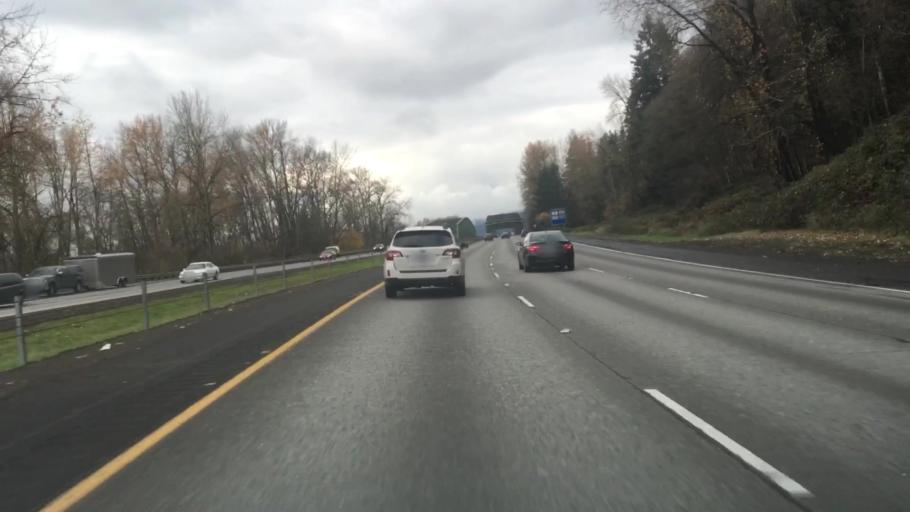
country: US
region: Washington
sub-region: Cowlitz County
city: Woodland
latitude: 45.8867
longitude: -122.7311
